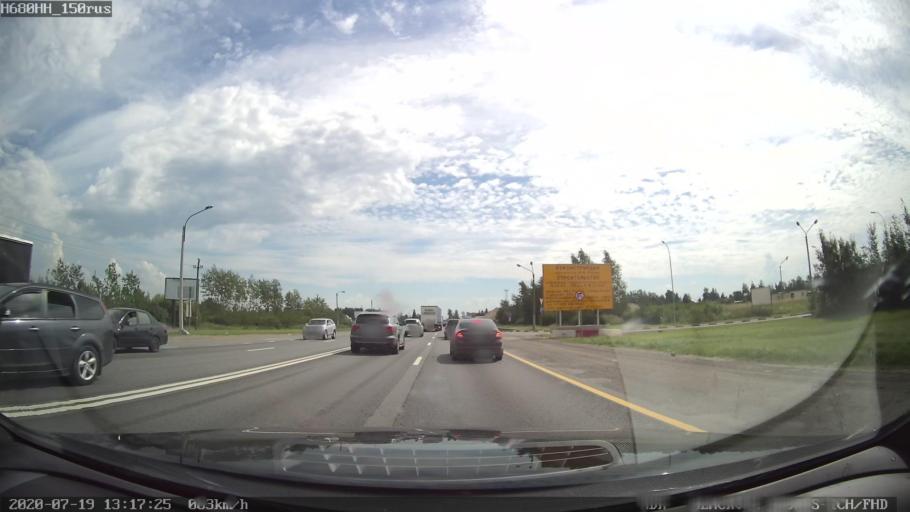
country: RU
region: St.-Petersburg
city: Kolpino
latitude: 59.7083
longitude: 30.5708
